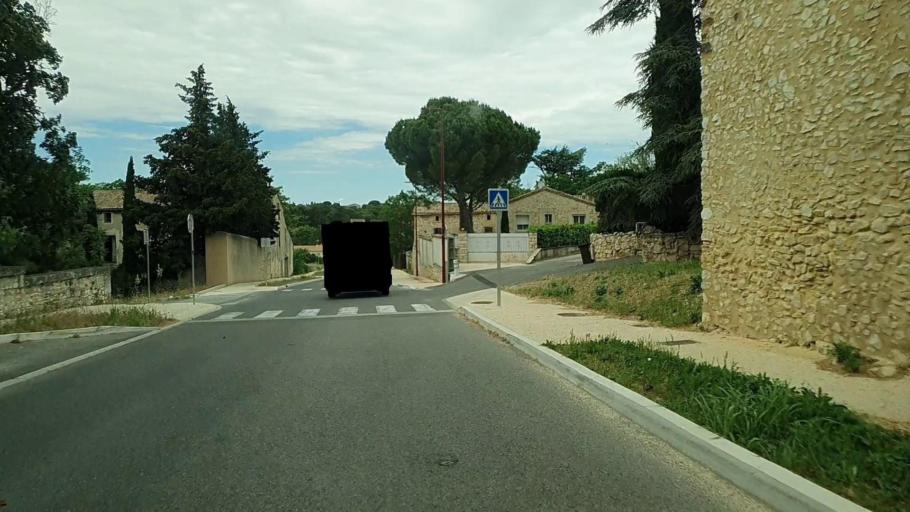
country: FR
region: Languedoc-Roussillon
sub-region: Departement du Gard
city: Connaux
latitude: 44.0426
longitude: 4.5800
